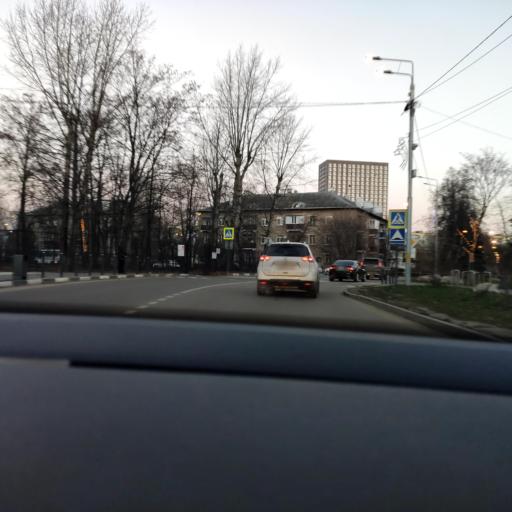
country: RU
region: Moskovskaya
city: Kotel'niki
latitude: 55.6607
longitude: 37.8528
